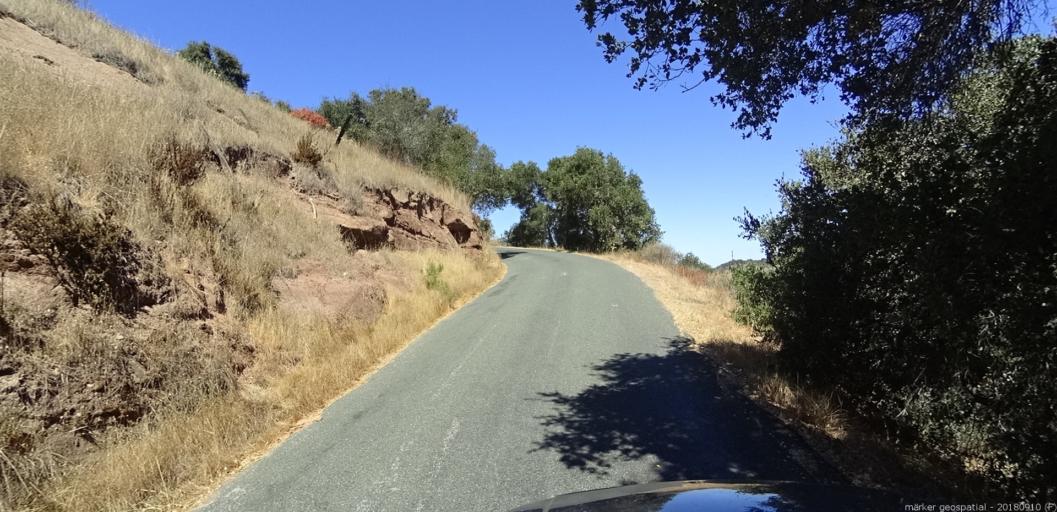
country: US
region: California
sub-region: Monterey County
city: Carmel Valley Village
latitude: 36.4836
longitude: -121.8058
